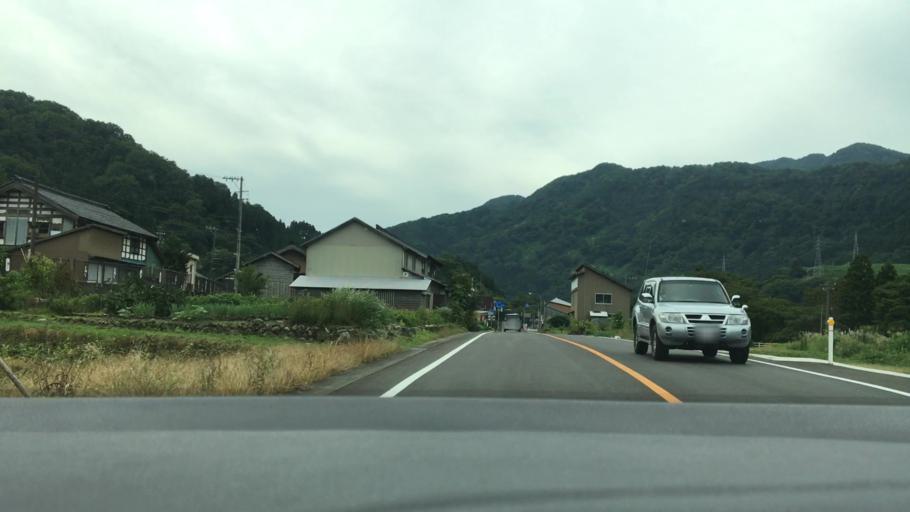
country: JP
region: Ishikawa
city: Tsurugi-asahimachi
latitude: 36.3084
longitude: 136.6436
